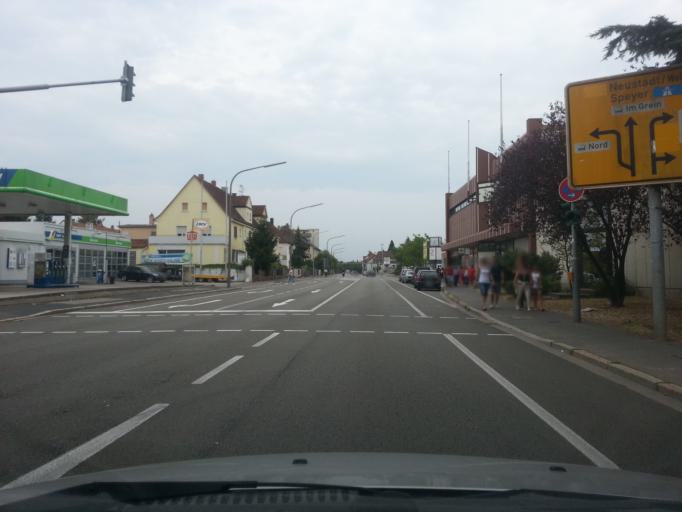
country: DE
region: Rheinland-Pfalz
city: Landau in der Pfalz
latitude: 49.2013
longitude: 8.1245
